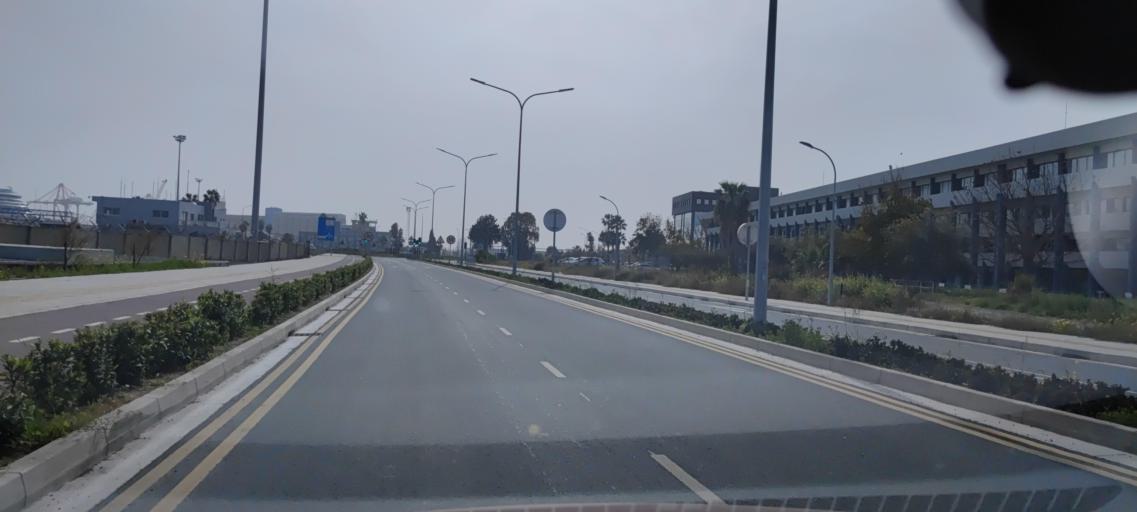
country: CY
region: Limassol
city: Limassol
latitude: 34.6604
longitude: 33.0221
